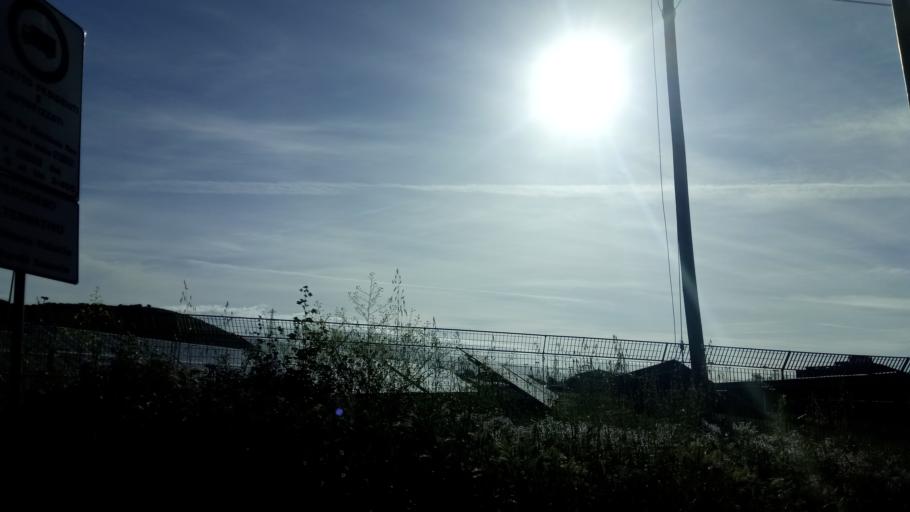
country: IT
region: Latium
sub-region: Provincia di Latina
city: Minturno
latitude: 41.2556
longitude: 13.7543
